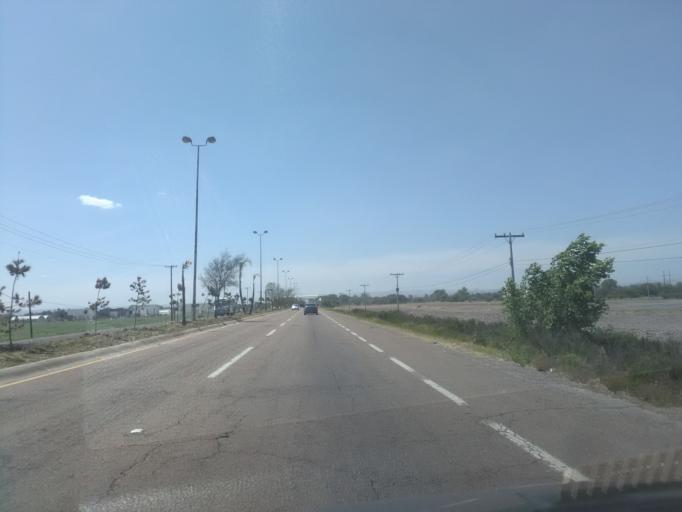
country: MX
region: Durango
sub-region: Durango
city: Jose Refugio Salcido
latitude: 24.0236
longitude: -104.5476
